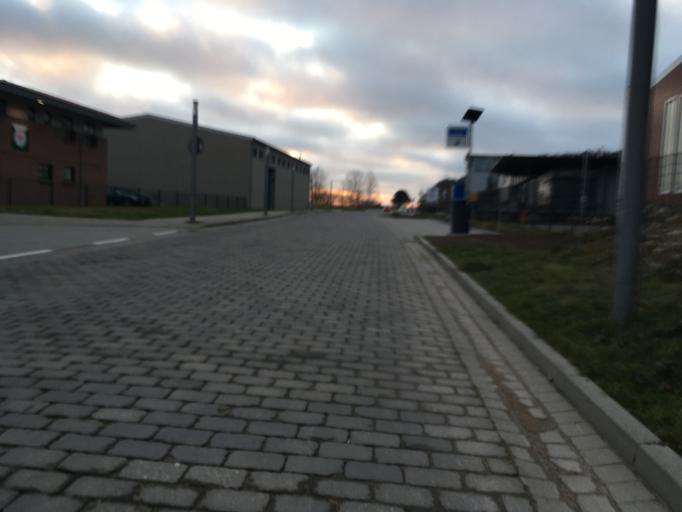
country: DE
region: Mecklenburg-Vorpommern
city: Sassnitz
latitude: 54.5092
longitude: 13.6338
